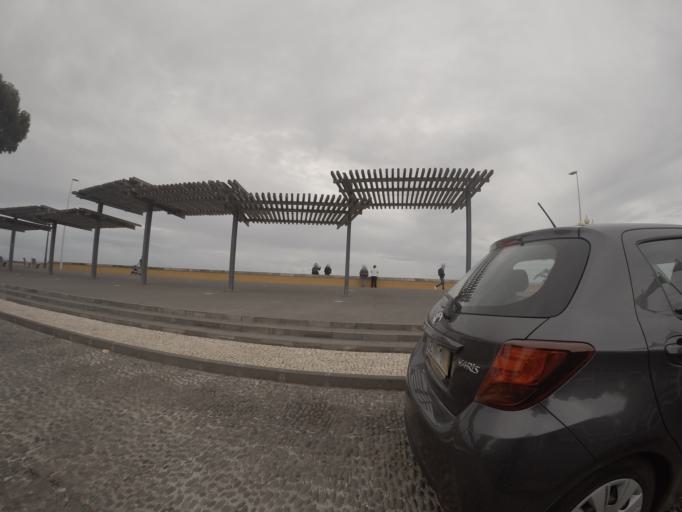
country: PT
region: Madeira
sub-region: Funchal
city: Funchal
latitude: 32.6470
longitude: -16.9025
